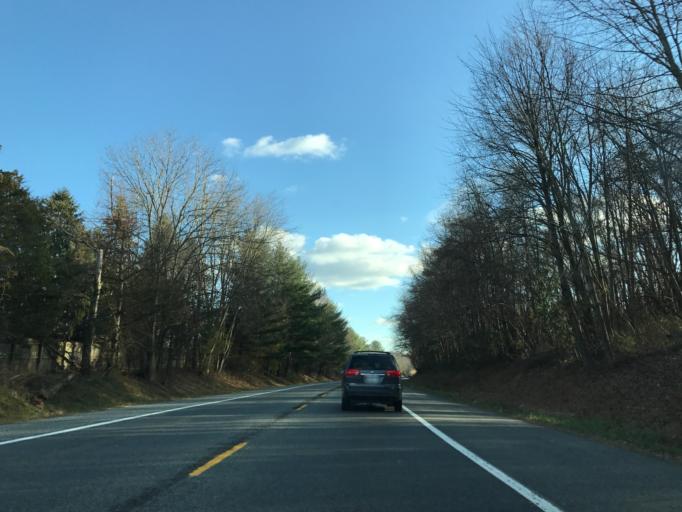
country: US
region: Maryland
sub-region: Harford County
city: Fallston
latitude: 39.5135
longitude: -76.4063
